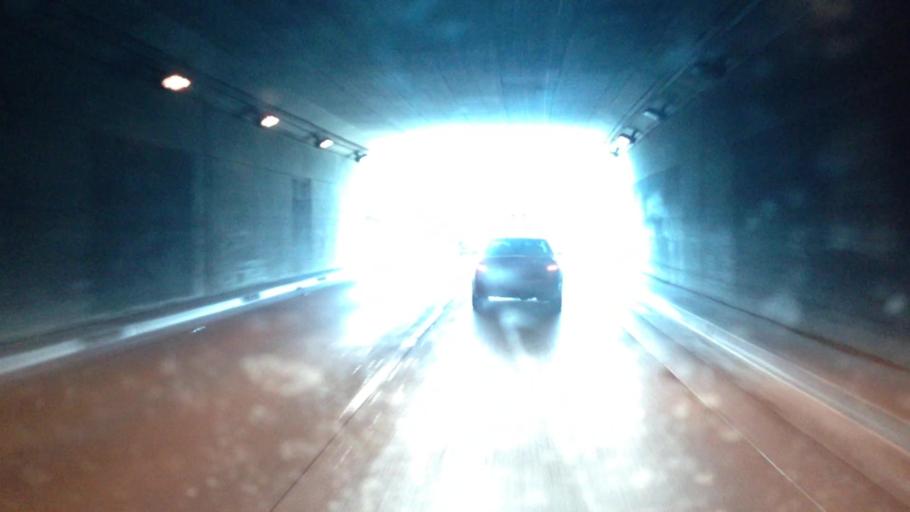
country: US
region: California
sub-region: Los Angeles County
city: Signal Hill
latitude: 33.8112
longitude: -118.1452
